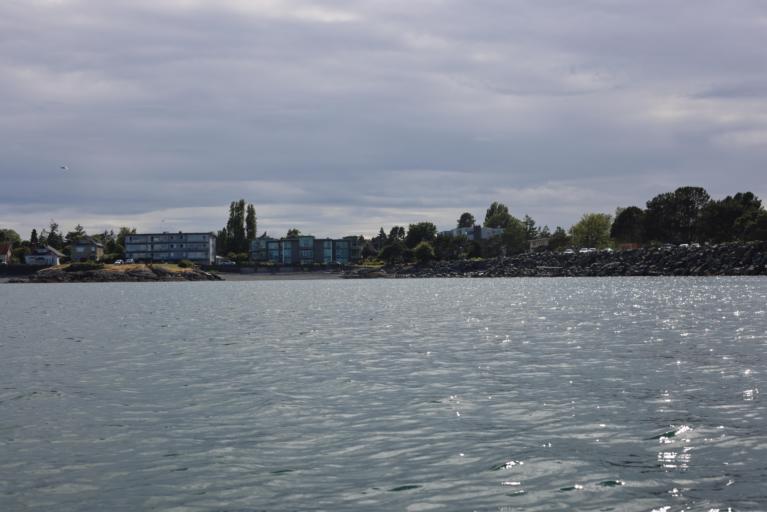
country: CA
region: British Columbia
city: Oak Bay
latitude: 48.4251
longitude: -123.2980
